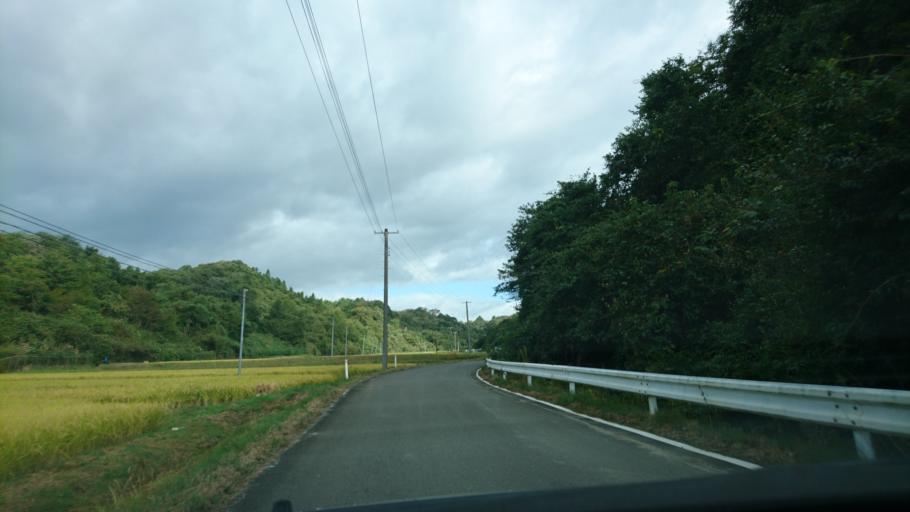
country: JP
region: Iwate
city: Ichinoseki
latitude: 38.8760
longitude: 141.0936
